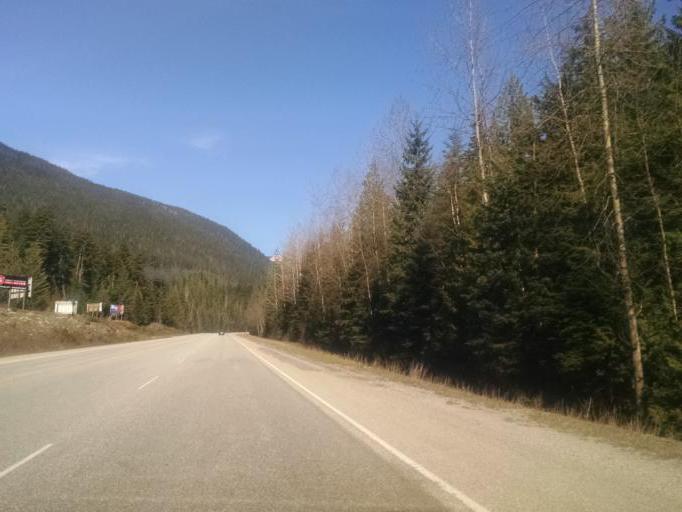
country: CA
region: British Columbia
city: Revelstoke
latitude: 51.0141
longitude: -118.0878
